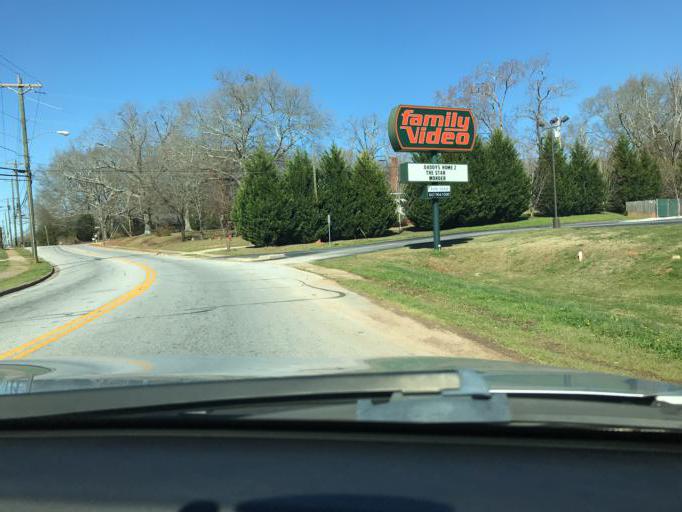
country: US
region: South Carolina
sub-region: Laurens County
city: Laurens
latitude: 34.4987
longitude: -81.9973
